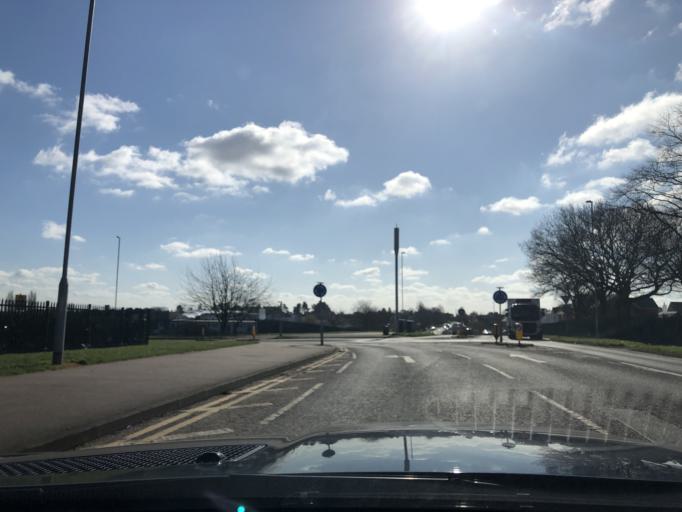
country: GB
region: England
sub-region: Northamptonshire
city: Northampton
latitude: 52.2629
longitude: -0.8501
